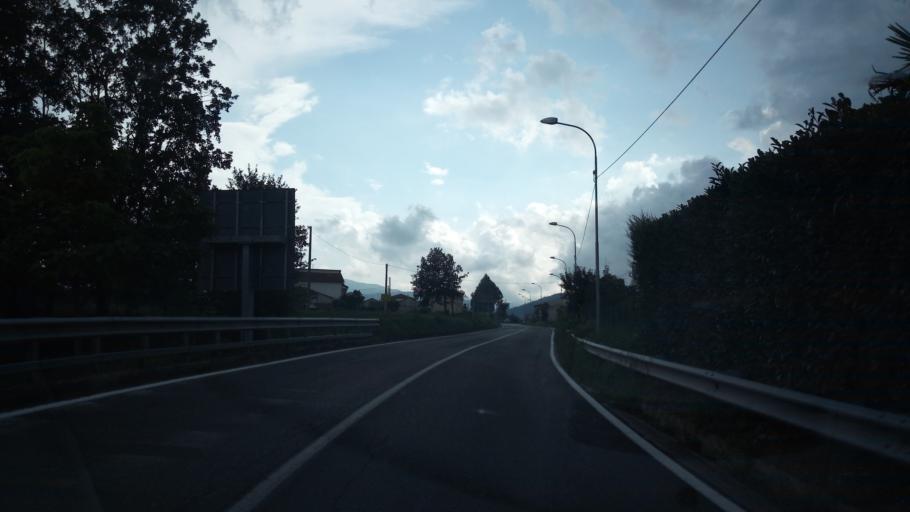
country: IT
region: Campania
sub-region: Provincia di Salerno
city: Buonabitacolo
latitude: 40.2845
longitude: 15.6353
